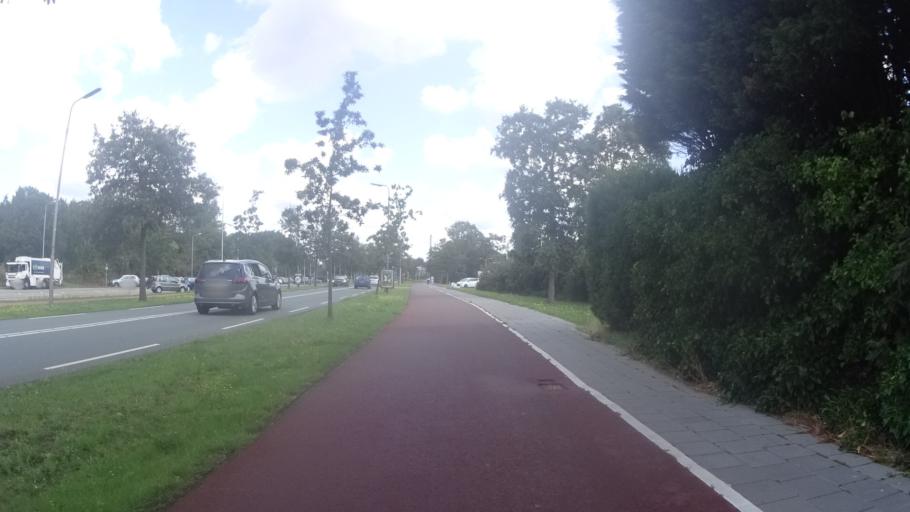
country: NL
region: North Holland
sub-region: Gemeente Velsen
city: Velsen-Zuid
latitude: 52.4544
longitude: 4.6335
